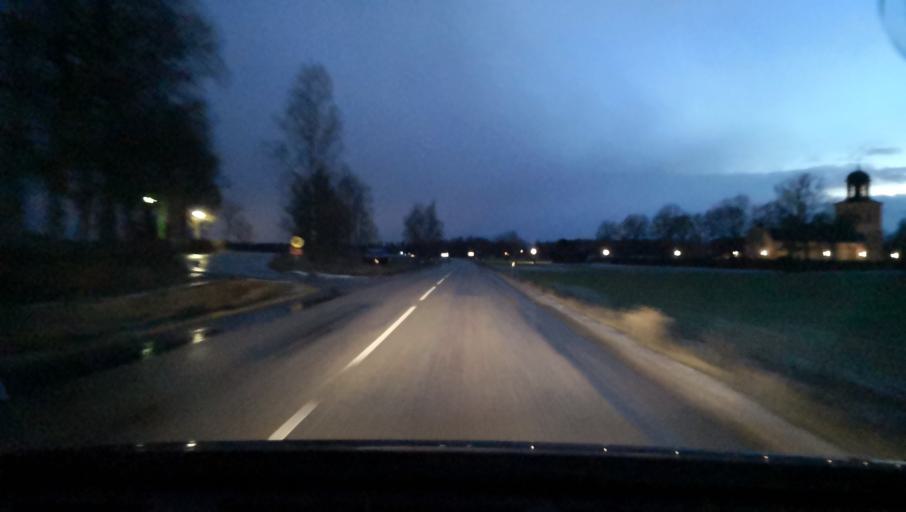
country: SE
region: Vaestmanland
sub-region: Vasteras
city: Skultuna
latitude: 59.7735
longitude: 16.4613
